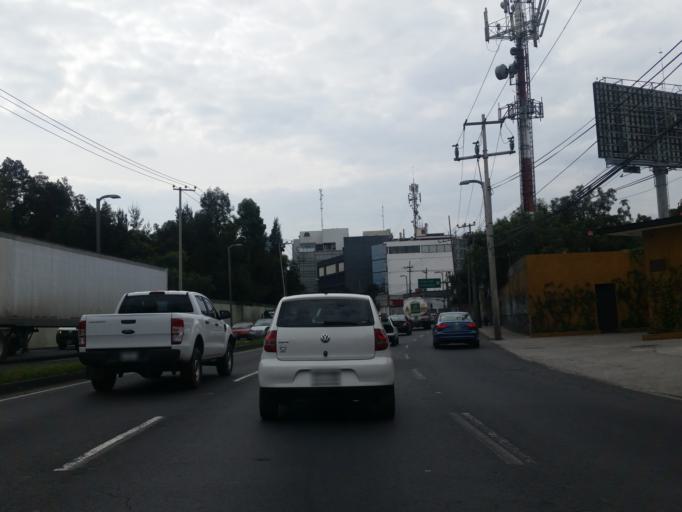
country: MX
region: Mexico City
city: Polanco
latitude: 19.3950
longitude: -99.2312
